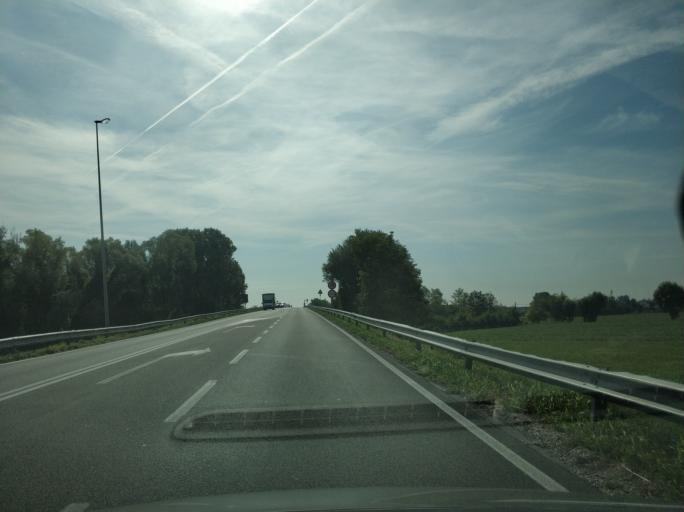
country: IT
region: Veneto
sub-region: Provincia di Padova
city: Pozzonovo
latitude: 45.2108
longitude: 11.7718
